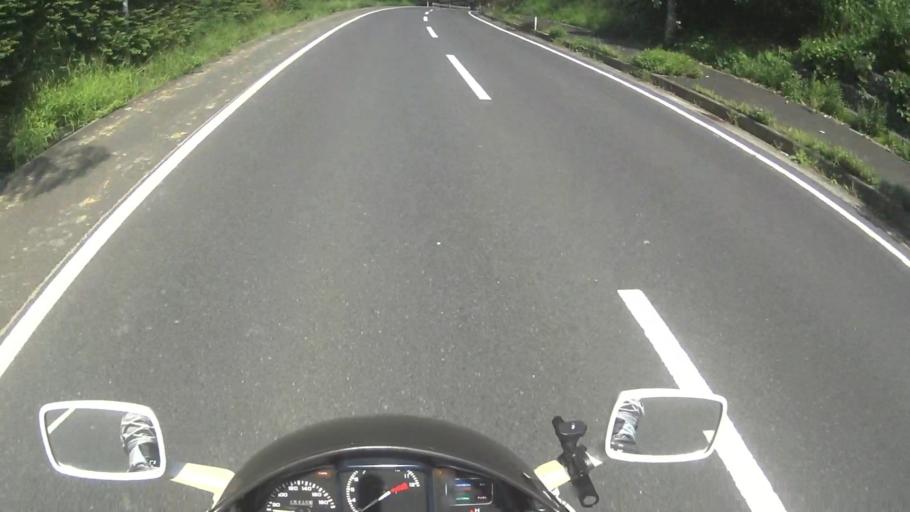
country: JP
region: Kyoto
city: Miyazu
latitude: 35.6648
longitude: 135.2612
